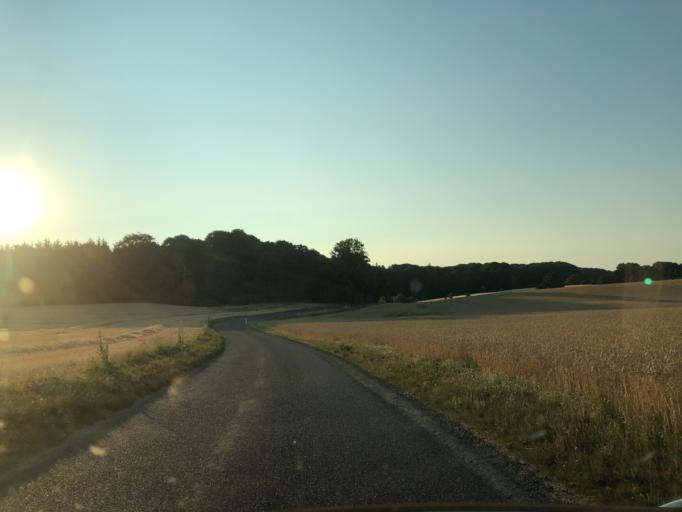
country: DK
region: Central Jutland
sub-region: Skanderborg Kommune
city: Skanderborg
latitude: 56.0875
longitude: 9.8738
